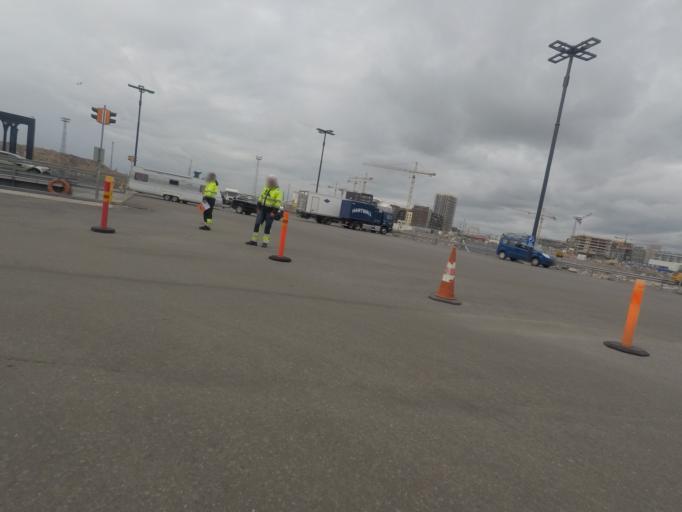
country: FI
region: Uusimaa
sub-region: Helsinki
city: Helsinki
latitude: 60.1498
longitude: 24.9143
